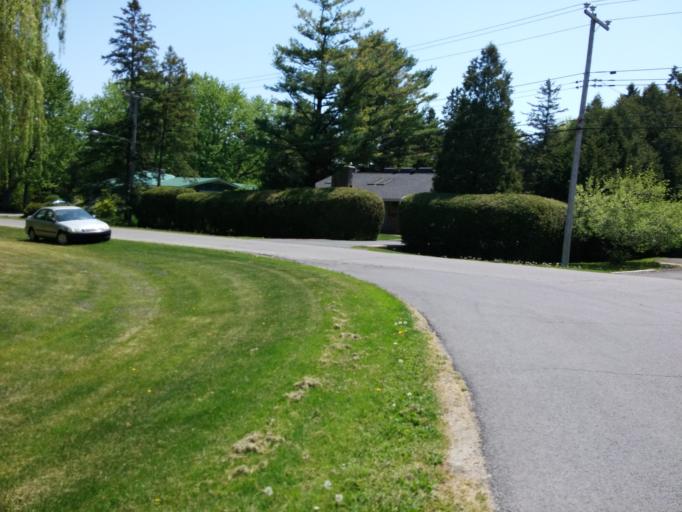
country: CA
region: Quebec
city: Baie-D'Urfe
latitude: 45.4202
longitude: -73.8993
